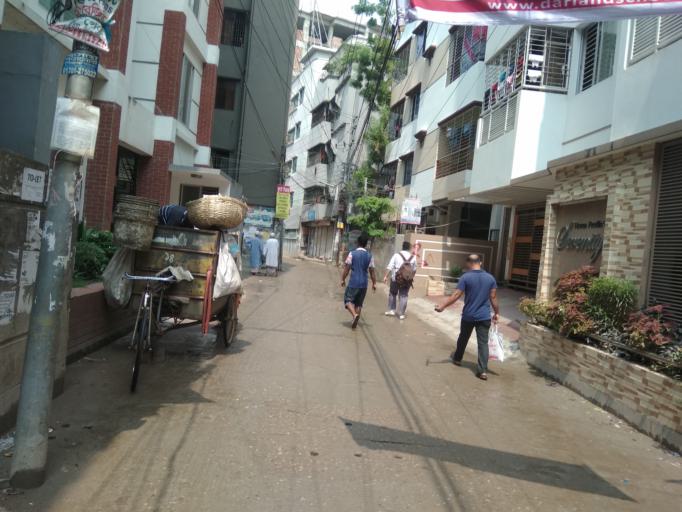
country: BD
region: Dhaka
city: Azimpur
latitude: 23.7996
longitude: 90.3743
